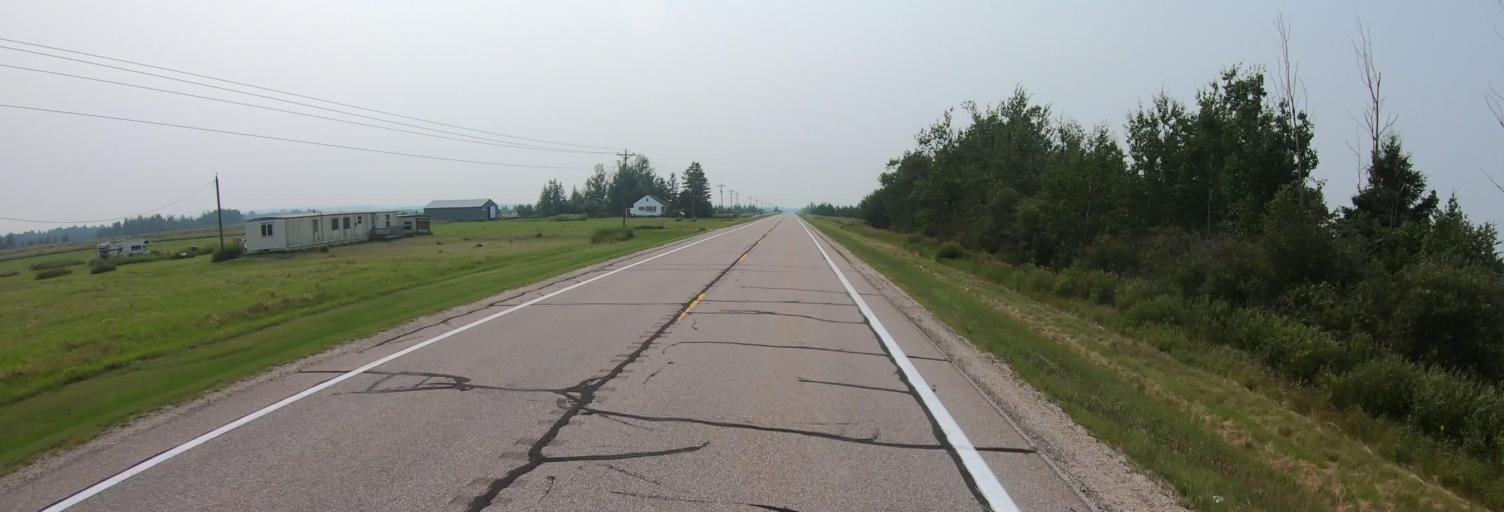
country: US
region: Michigan
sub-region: Chippewa County
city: Sault Ste. Marie
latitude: 46.1291
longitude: -84.2817
